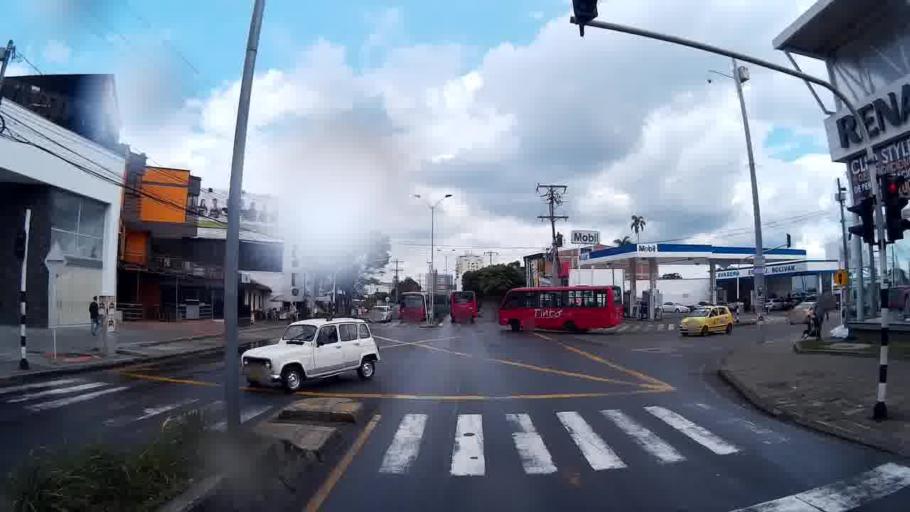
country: CO
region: Quindio
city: Calarca
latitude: 4.5577
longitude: -75.6563
